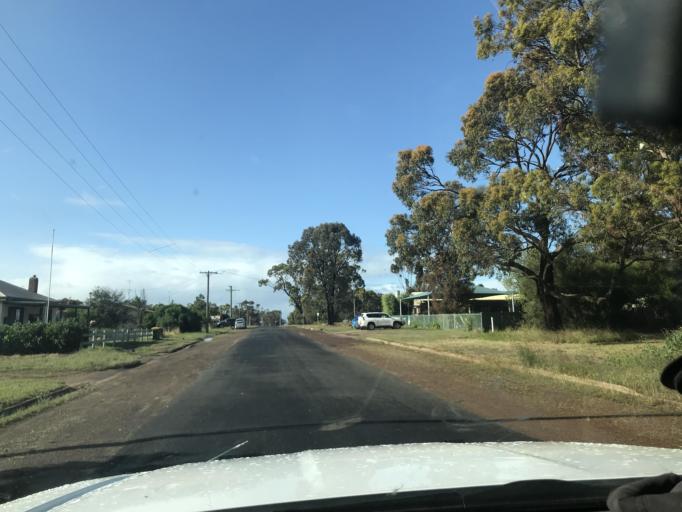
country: AU
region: Victoria
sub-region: Horsham
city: Horsham
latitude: -36.7189
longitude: 141.4770
